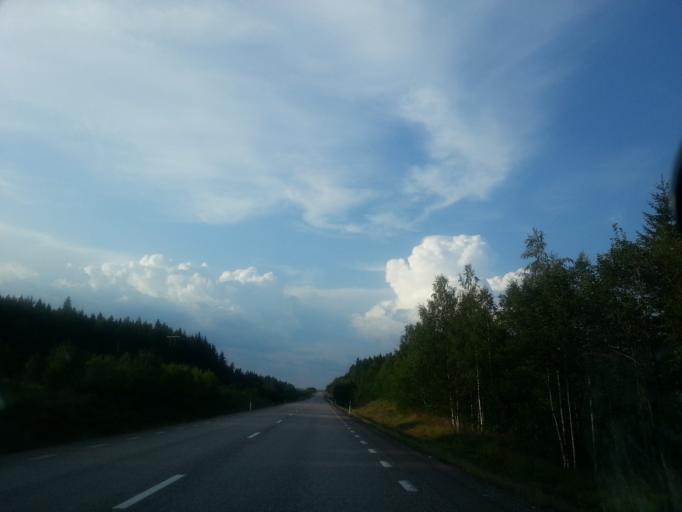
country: SE
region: Dalarna
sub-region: Avesta Kommun
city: Horndal
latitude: 60.2405
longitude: 16.3542
